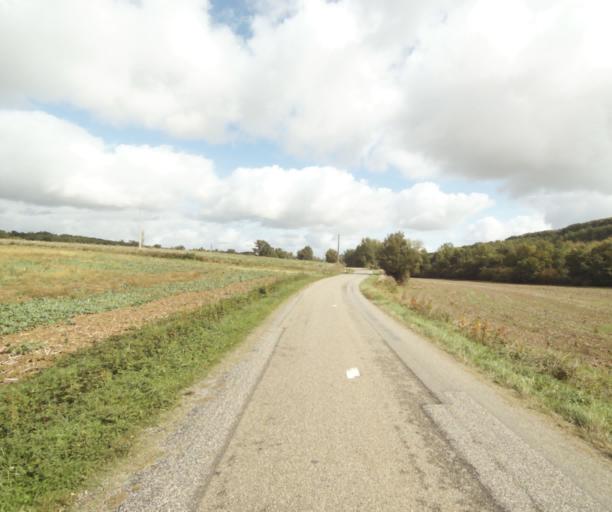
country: FR
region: Midi-Pyrenees
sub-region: Departement du Tarn-et-Garonne
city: Finhan
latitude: 43.8744
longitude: 1.1296
